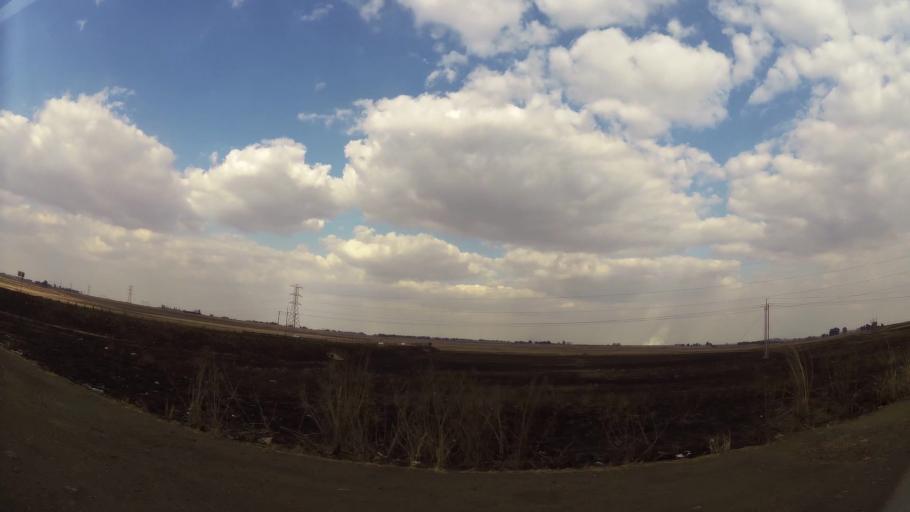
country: ZA
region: Mpumalanga
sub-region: Nkangala District Municipality
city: Delmas
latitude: -26.1750
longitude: 28.6982
